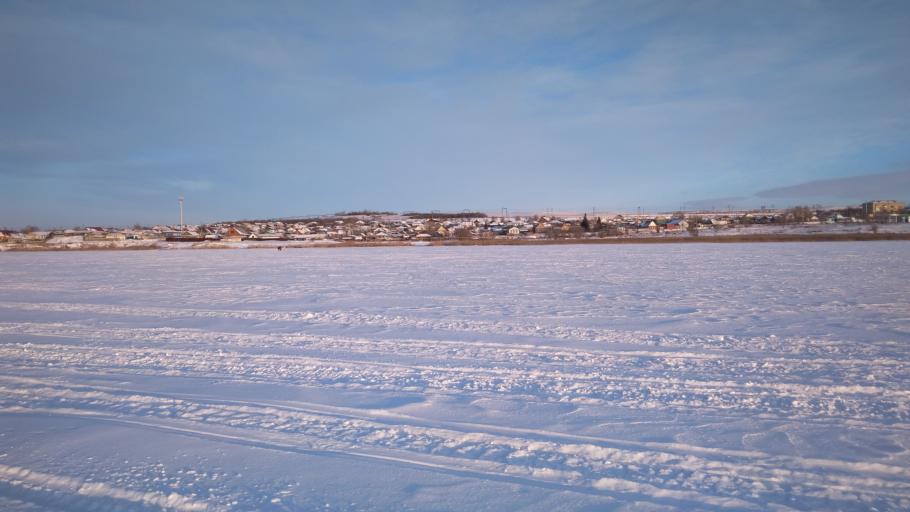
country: RU
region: Chelyabinsk
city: Troitsk
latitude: 54.0846
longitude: 61.5861
